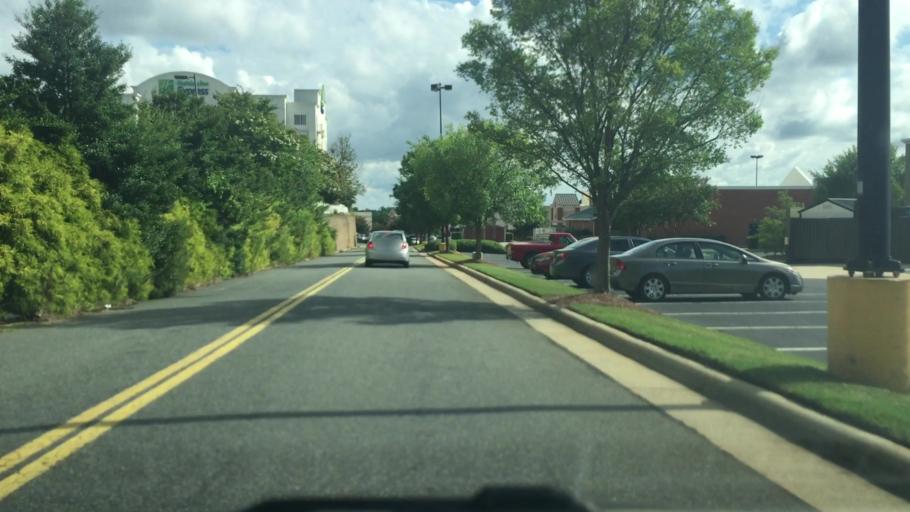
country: US
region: North Carolina
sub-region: Iredell County
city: Mooresville
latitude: 35.5922
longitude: -80.8573
